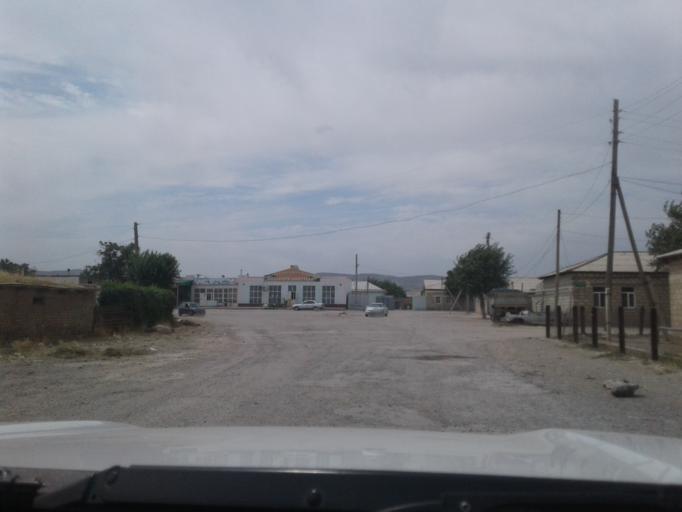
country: TM
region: Balkan
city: Serdar
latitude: 38.9901
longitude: 56.2682
